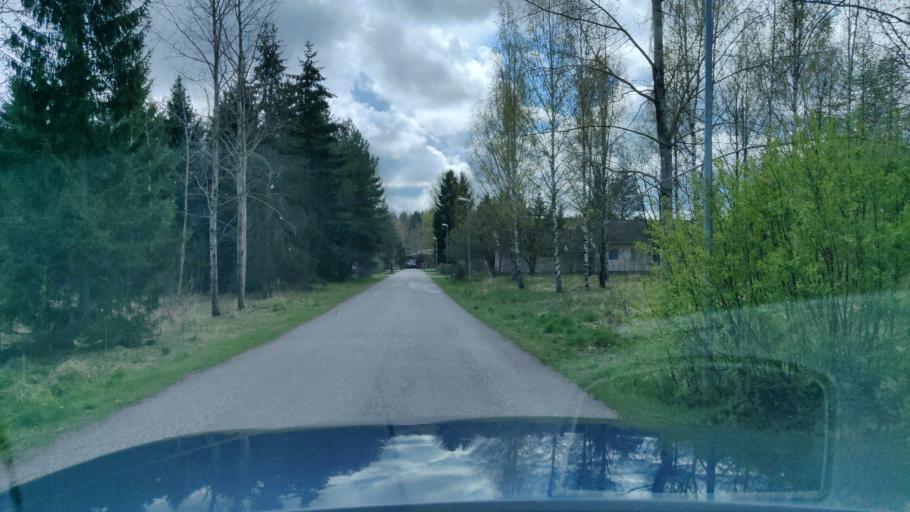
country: FI
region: Uusimaa
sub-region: Helsinki
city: Nurmijaervi
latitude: 60.3635
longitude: 24.7417
